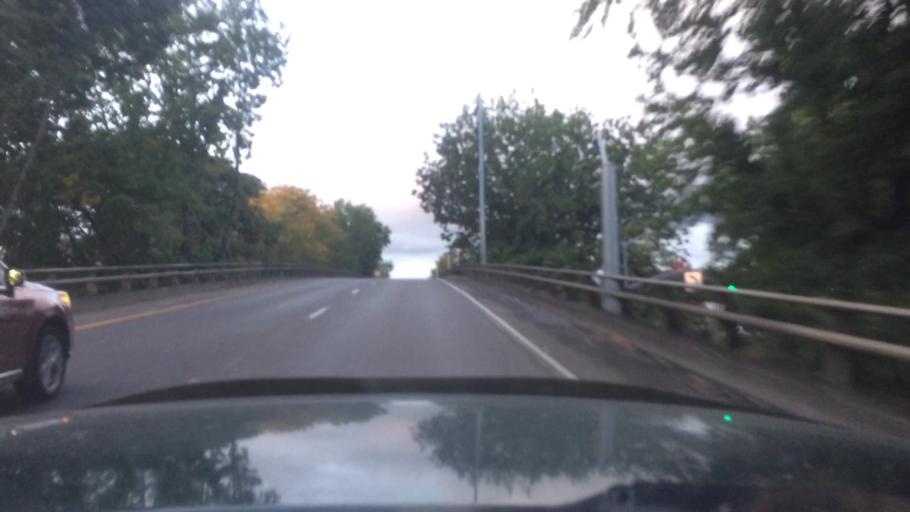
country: US
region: Oregon
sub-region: Lane County
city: Eugene
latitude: 44.0530
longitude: -123.1005
